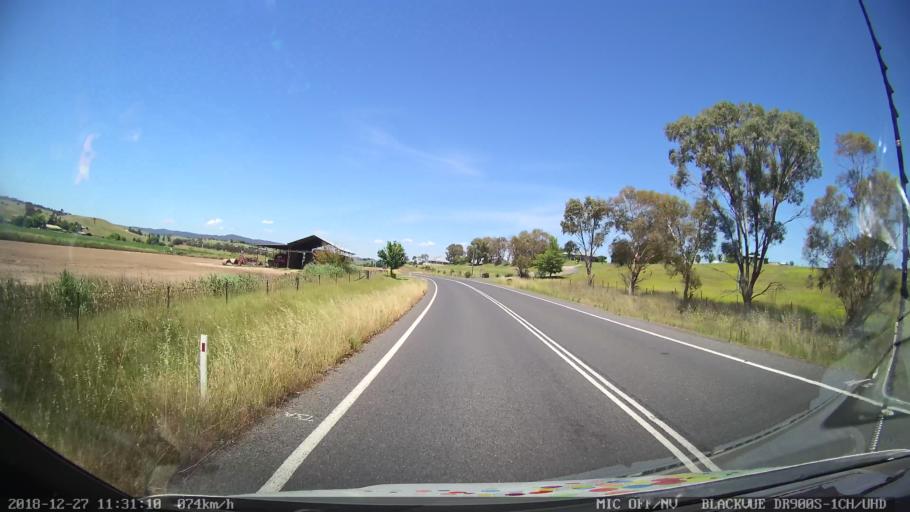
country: AU
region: New South Wales
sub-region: Bathurst Regional
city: Perthville
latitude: -33.4924
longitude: 149.5404
